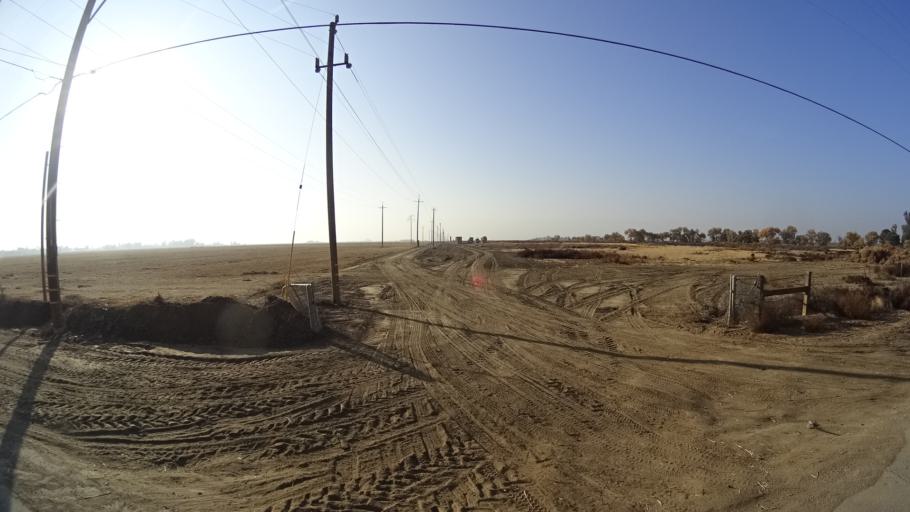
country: US
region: California
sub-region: Kern County
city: Greenfield
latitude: 35.2525
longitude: -118.9763
